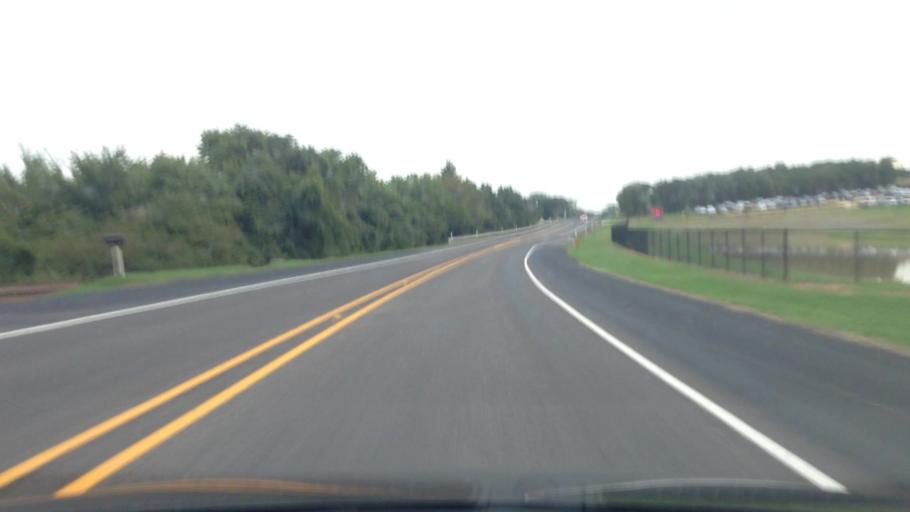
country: US
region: Texas
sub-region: Johnson County
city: Joshua
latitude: 32.4815
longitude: -97.3394
